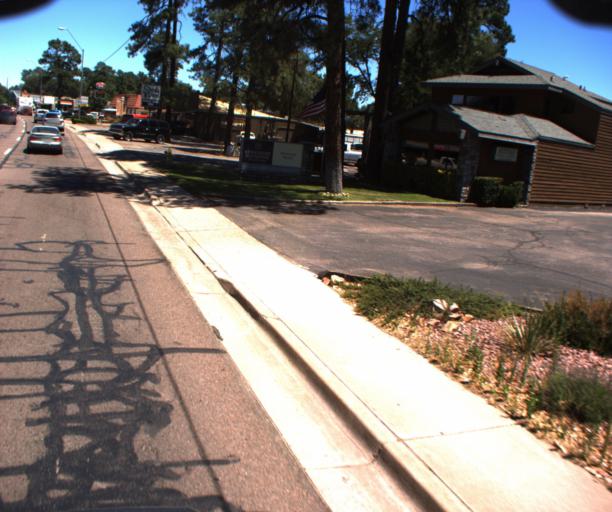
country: US
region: Arizona
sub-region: Gila County
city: Payson
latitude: 34.2328
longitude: -111.3237
